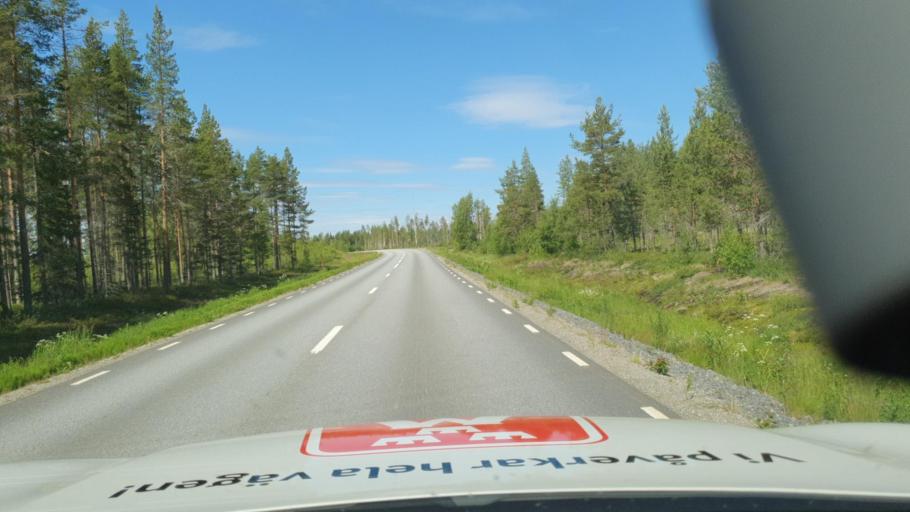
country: SE
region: Vaesterbotten
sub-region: Skelleftea Kommun
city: Forsbacka
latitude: 64.7316
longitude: 20.3924
